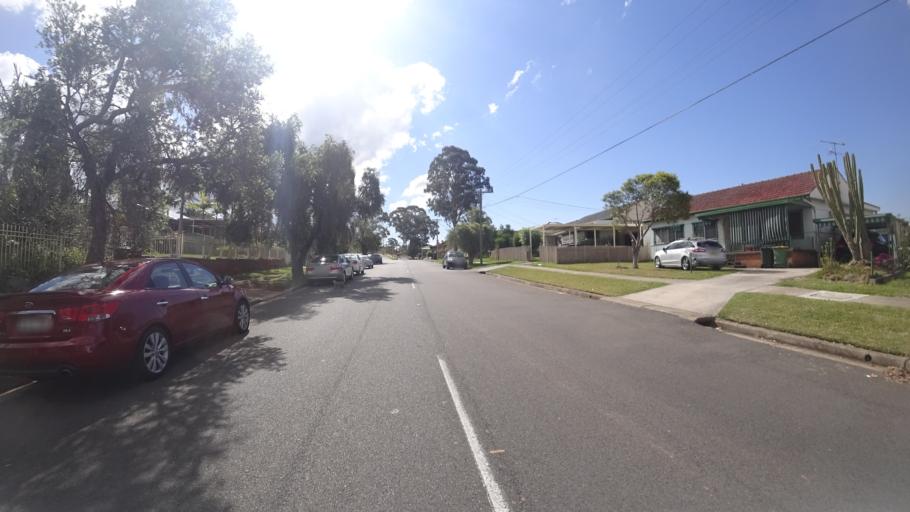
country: AU
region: New South Wales
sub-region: Fairfield
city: Cabramatta West
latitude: -33.9109
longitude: 150.9055
